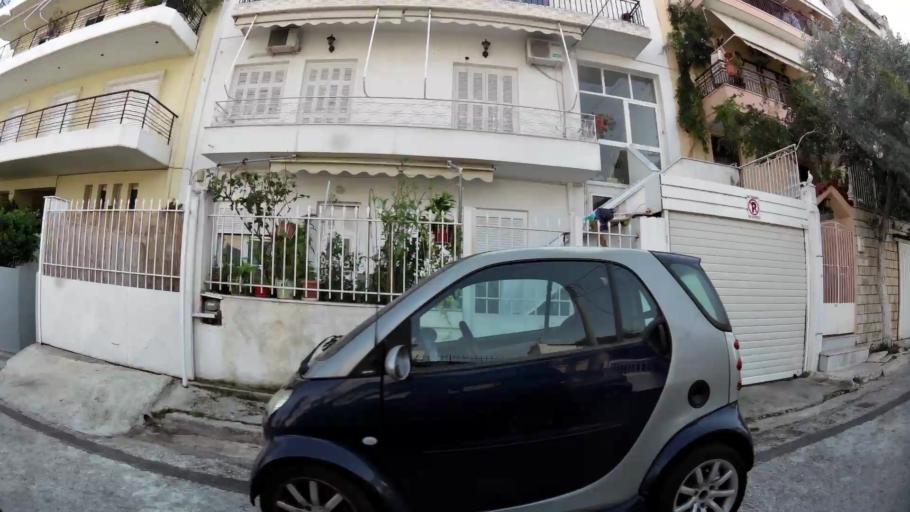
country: GR
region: Attica
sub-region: Nomarchia Athinas
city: Galatsi
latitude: 38.0088
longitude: 23.7546
